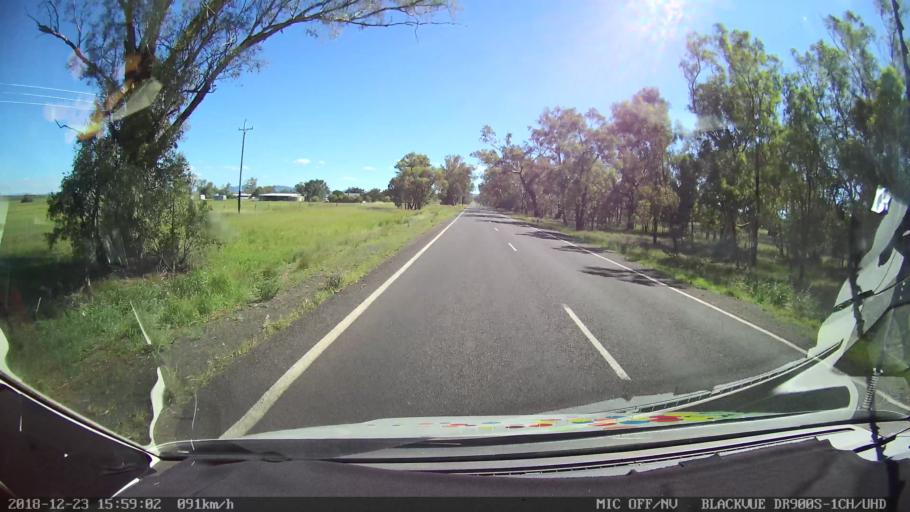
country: AU
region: New South Wales
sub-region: Tamworth Municipality
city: Phillip
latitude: -31.1952
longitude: 150.8366
